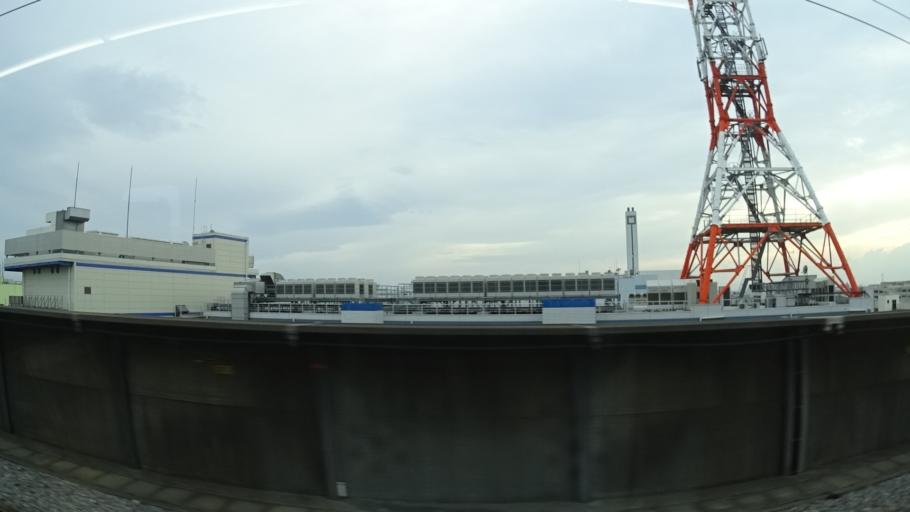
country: JP
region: Saitama
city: Shimotoda
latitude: 35.8331
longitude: 139.6541
